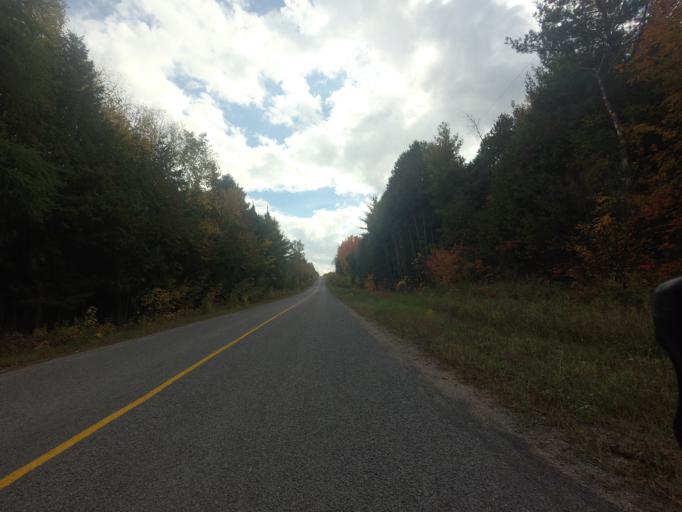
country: CA
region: Ontario
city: Pembroke
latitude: 45.5789
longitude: -77.1311
